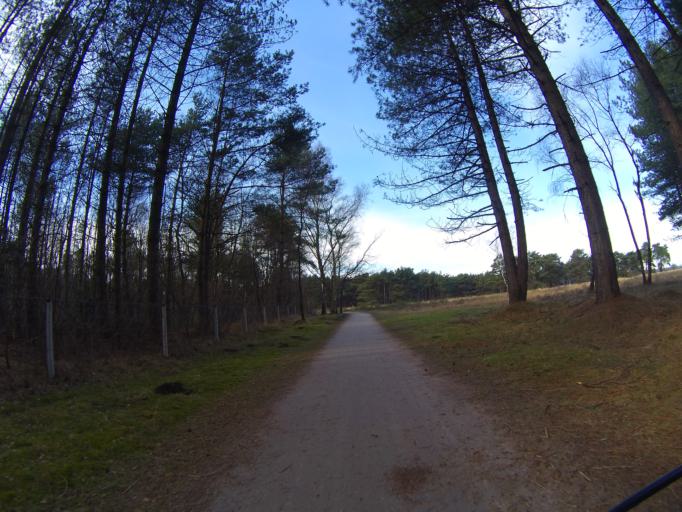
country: NL
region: North Holland
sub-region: Gemeente Hilversum
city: Hilversum
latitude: 52.2437
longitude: 5.1835
